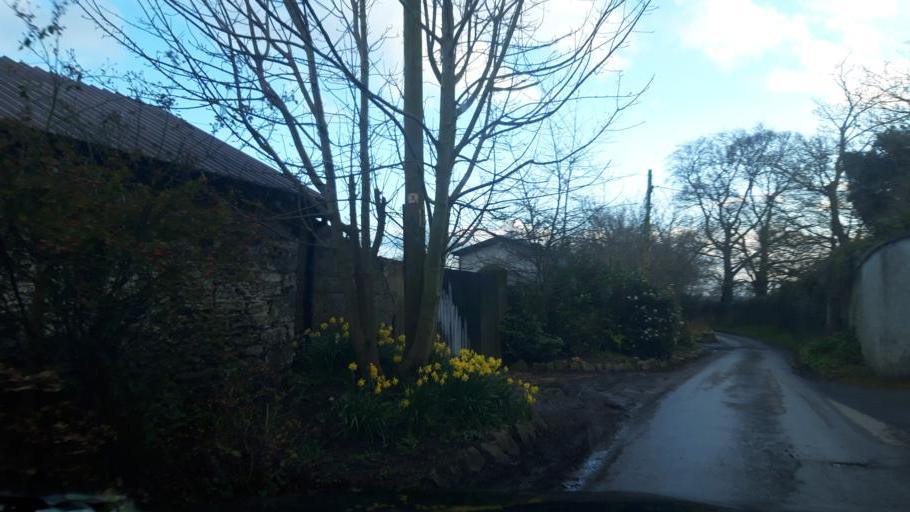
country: IE
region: Leinster
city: Donabate
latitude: 53.4718
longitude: -6.1716
